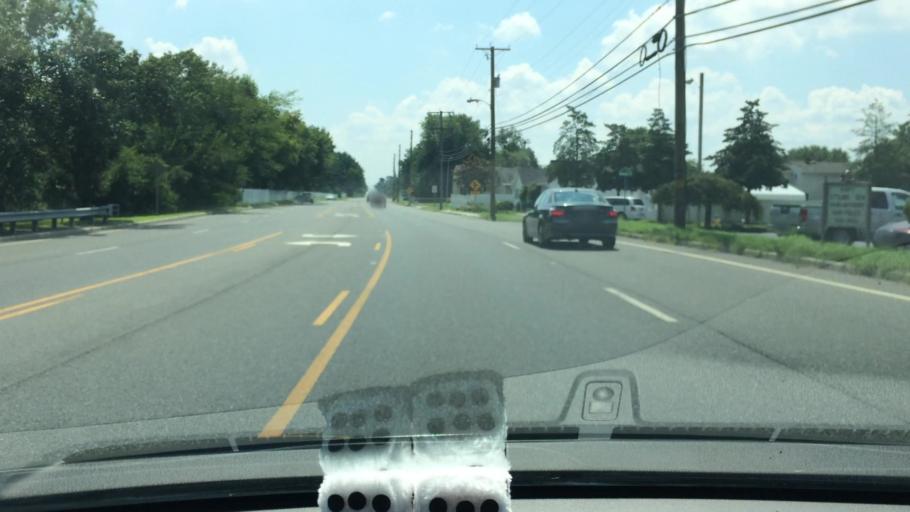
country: US
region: New Jersey
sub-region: Gloucester County
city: Turnersville
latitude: 39.7620
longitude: -75.0850
